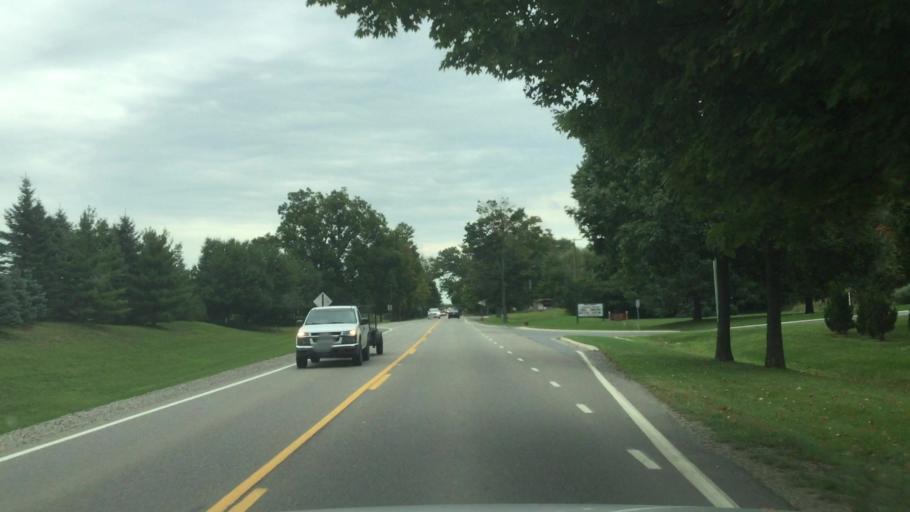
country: US
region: Michigan
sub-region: Livingston County
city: Whitmore Lake
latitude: 42.4639
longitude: -83.7729
